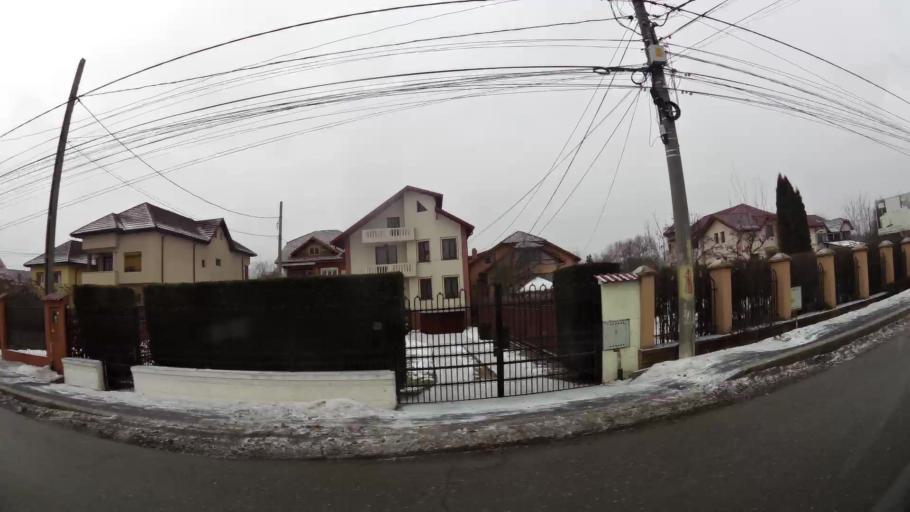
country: RO
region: Dambovita
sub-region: Municipiul Targoviste
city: Targoviste
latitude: 44.9374
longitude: 25.4687
